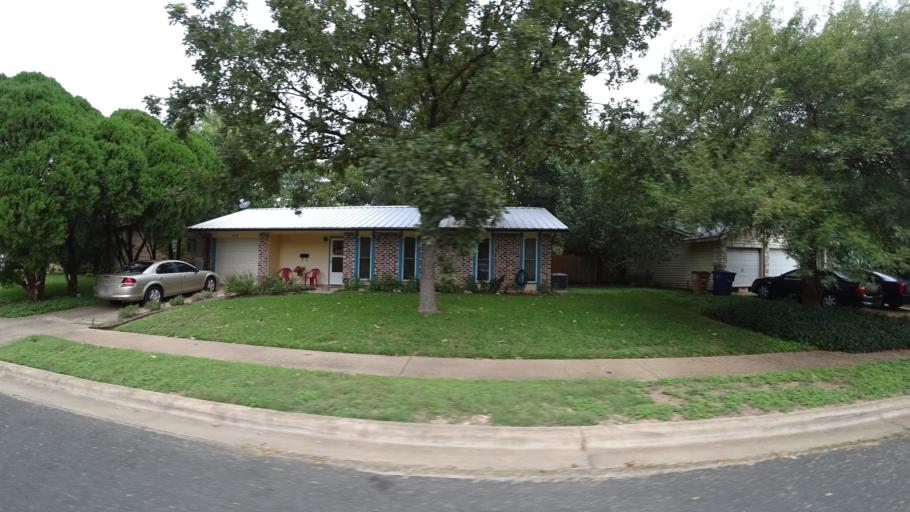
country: US
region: Texas
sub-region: Travis County
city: Rollingwood
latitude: 30.2149
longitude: -97.7815
